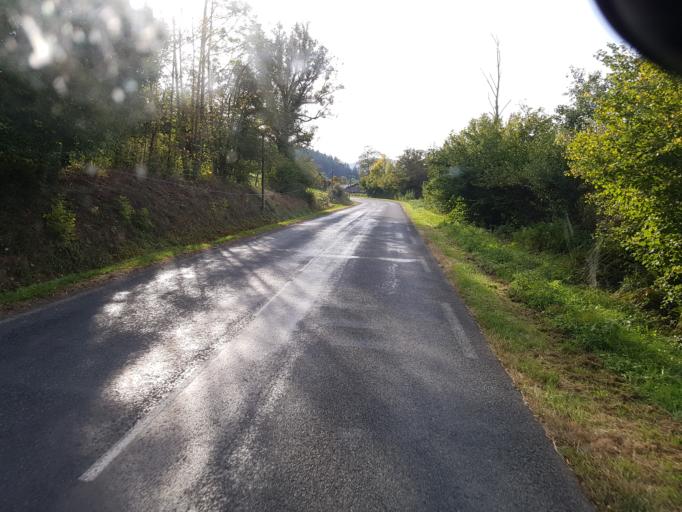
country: FR
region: Bourgogne
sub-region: Departement de Saone-et-Loire
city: Chauffailles
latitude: 46.2300
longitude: 4.4202
